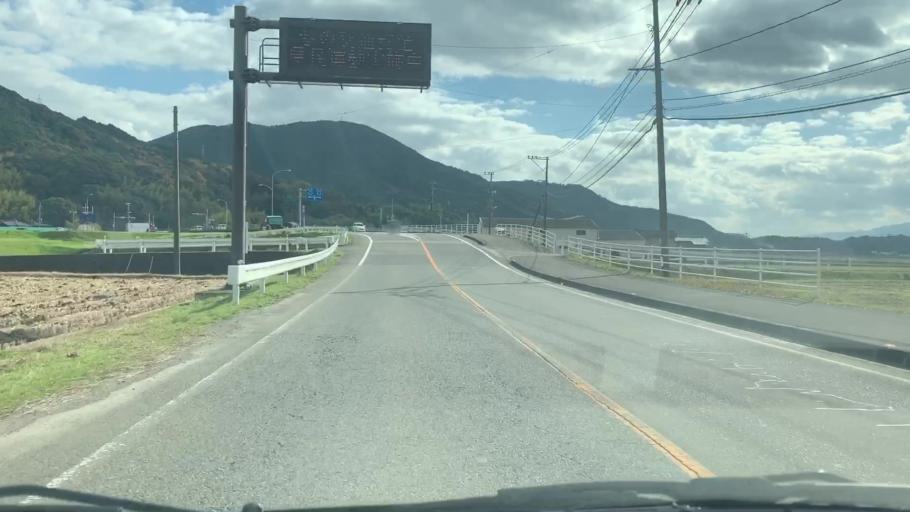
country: JP
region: Saga Prefecture
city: Takeocho-takeo
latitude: 33.2029
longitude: 130.0514
